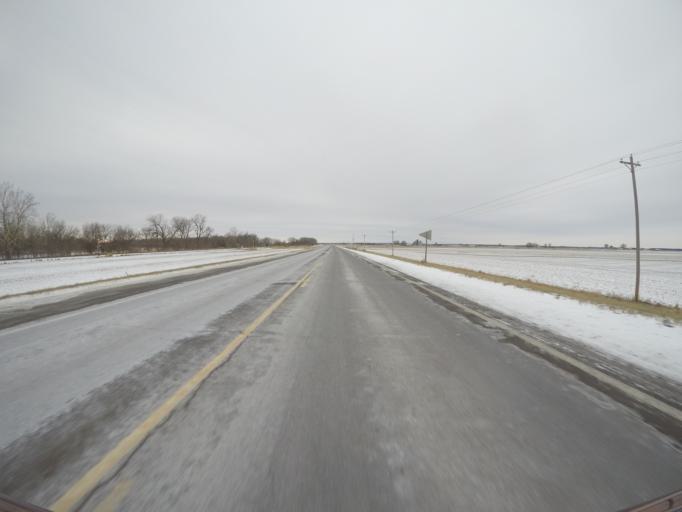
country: US
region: Kansas
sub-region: Pottawatomie County
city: Wamego
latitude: 39.2129
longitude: -96.2379
